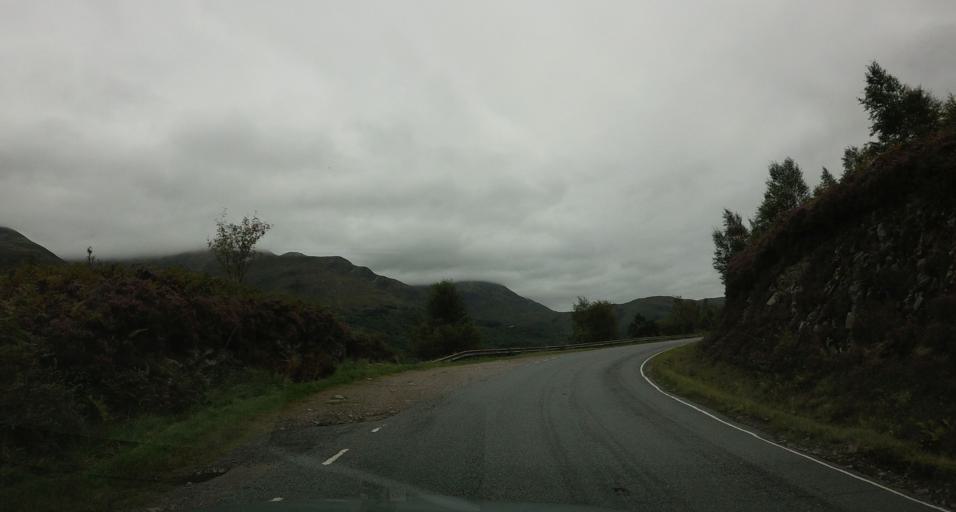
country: GB
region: Scotland
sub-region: Highland
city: Fort William
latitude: 56.7093
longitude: -5.0030
